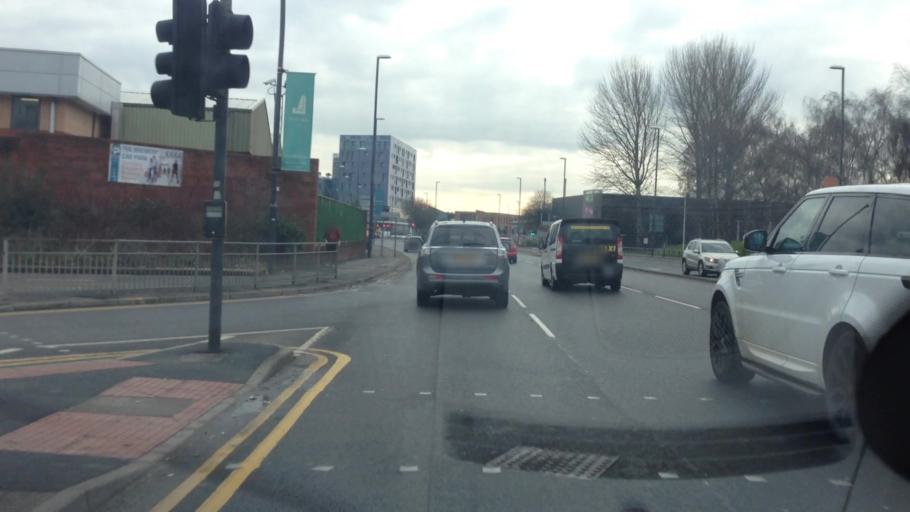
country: GB
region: England
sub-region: City and Borough of Leeds
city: Leeds
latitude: 53.7912
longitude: -1.5437
